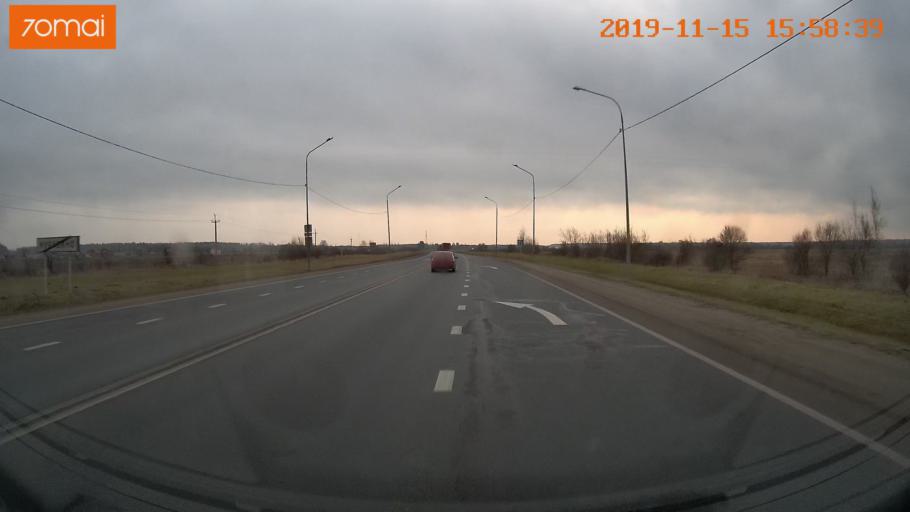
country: RU
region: Jaroslavl
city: Yaroslavl
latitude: 57.8172
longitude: 39.9528
